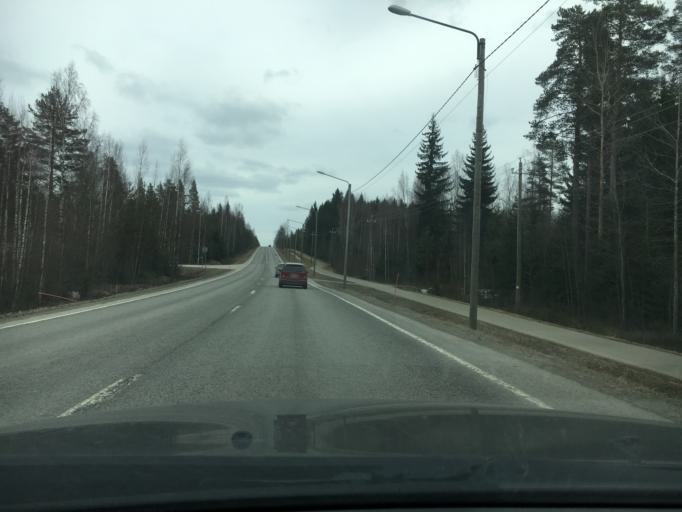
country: FI
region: Central Finland
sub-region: AEaenekoski
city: Suolahti
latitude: 62.5633
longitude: 25.8057
